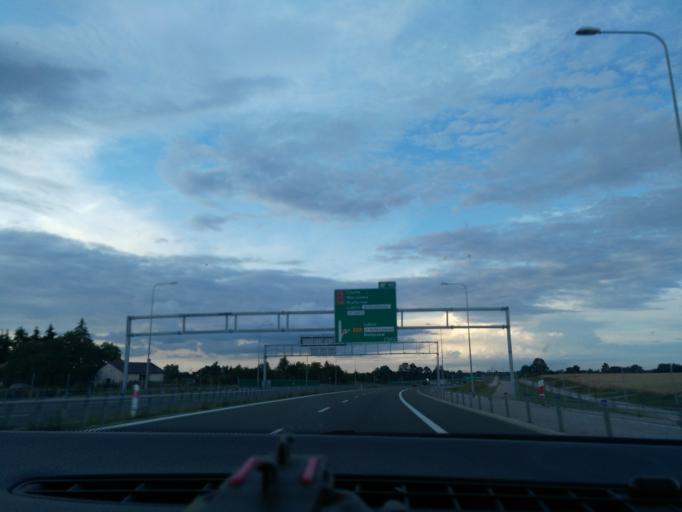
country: PL
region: Lublin Voivodeship
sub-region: Powiat lubelski
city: Kozubszczyzna
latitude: 51.2596
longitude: 22.4201
